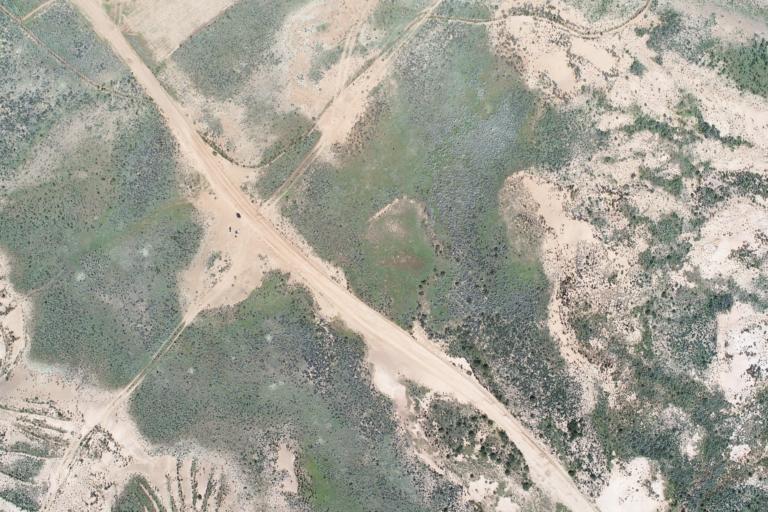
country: BO
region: La Paz
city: Curahuara de Carangas
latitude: -17.2915
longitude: -68.5112
